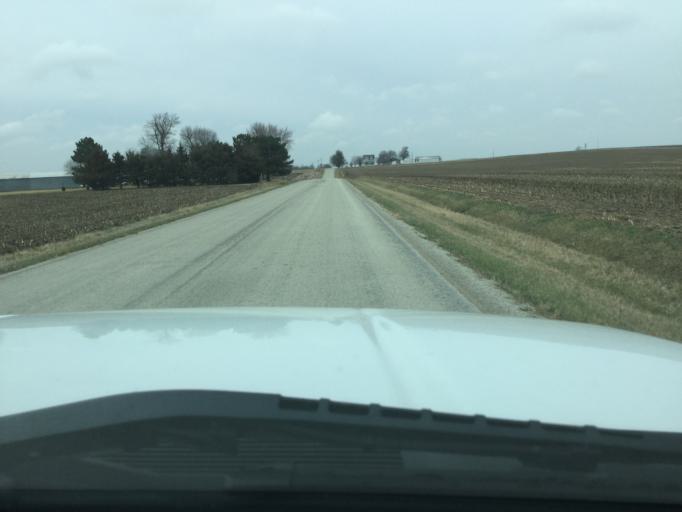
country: US
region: Kansas
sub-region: Nemaha County
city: Sabetha
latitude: 39.8462
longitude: -95.7142
